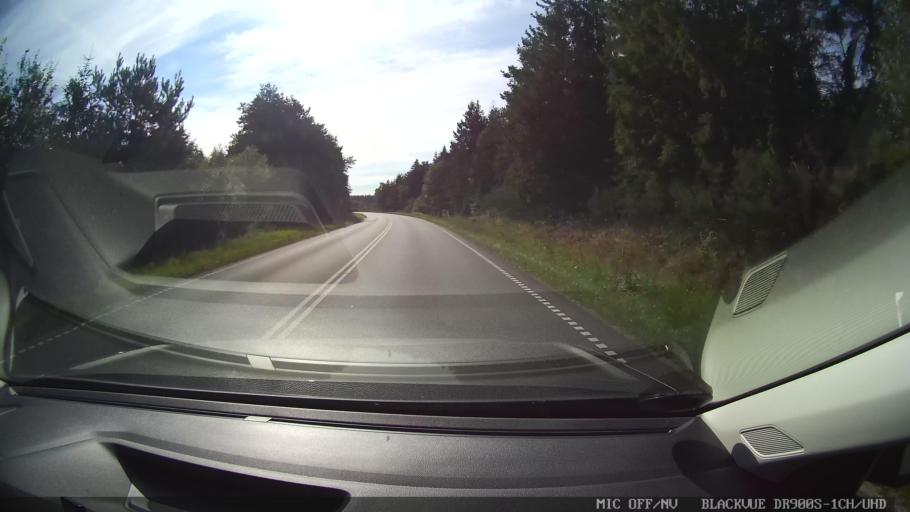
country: DK
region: North Denmark
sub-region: Mariagerfjord Kommune
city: Hadsund
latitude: 56.7337
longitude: 10.0797
